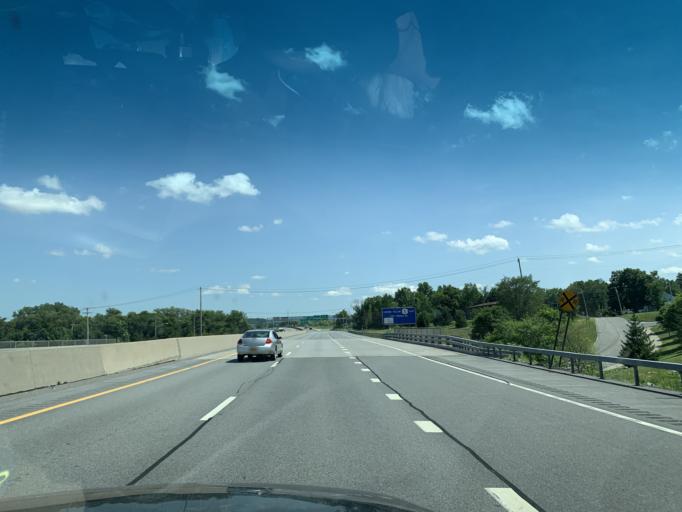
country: US
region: New York
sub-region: Oneida County
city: New Hartford
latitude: 43.0841
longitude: -75.2968
